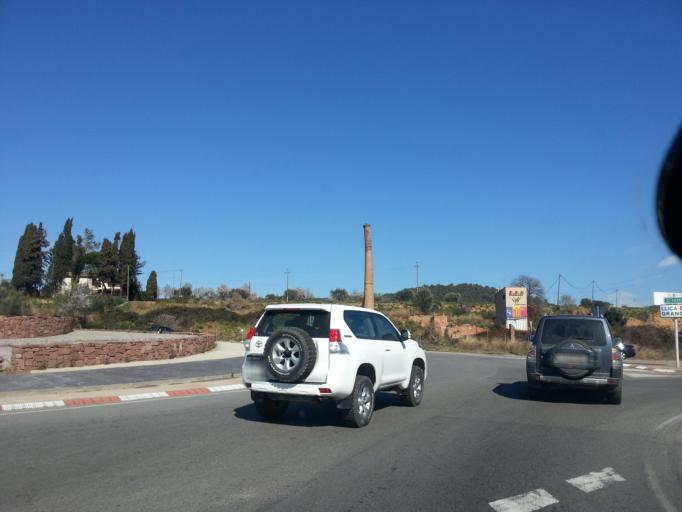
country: ES
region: Catalonia
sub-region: Provincia de Barcelona
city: Caldes de Montbui
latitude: 41.6327
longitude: 2.1743
